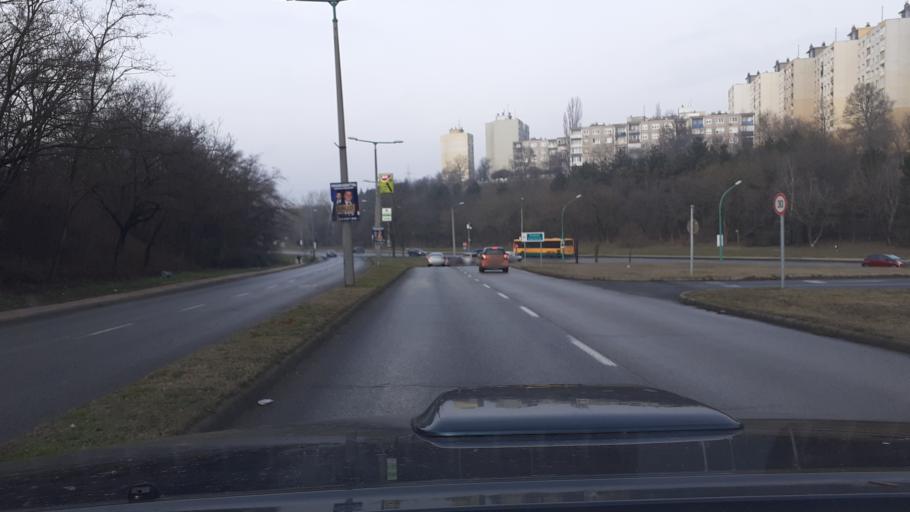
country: HU
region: Fejer
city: dunaujvaros
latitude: 46.9683
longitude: 18.9322
